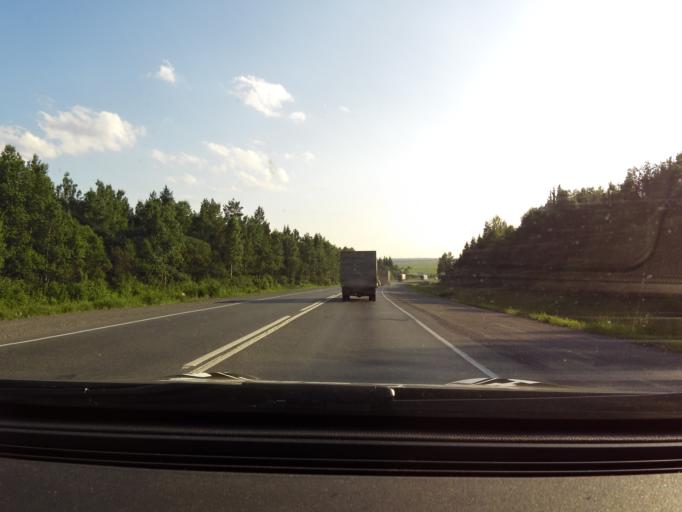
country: RU
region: Sverdlovsk
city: Druzhinino
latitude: 56.8119
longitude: 59.5559
